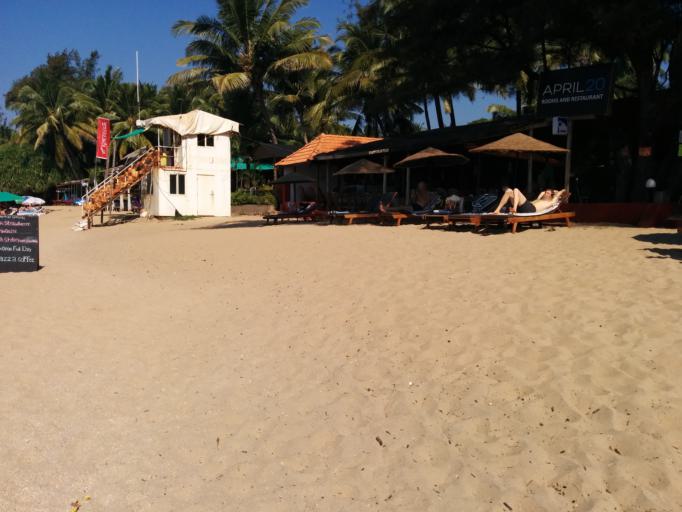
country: IN
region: Karnataka
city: Canacona
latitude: 14.9985
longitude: 74.0330
